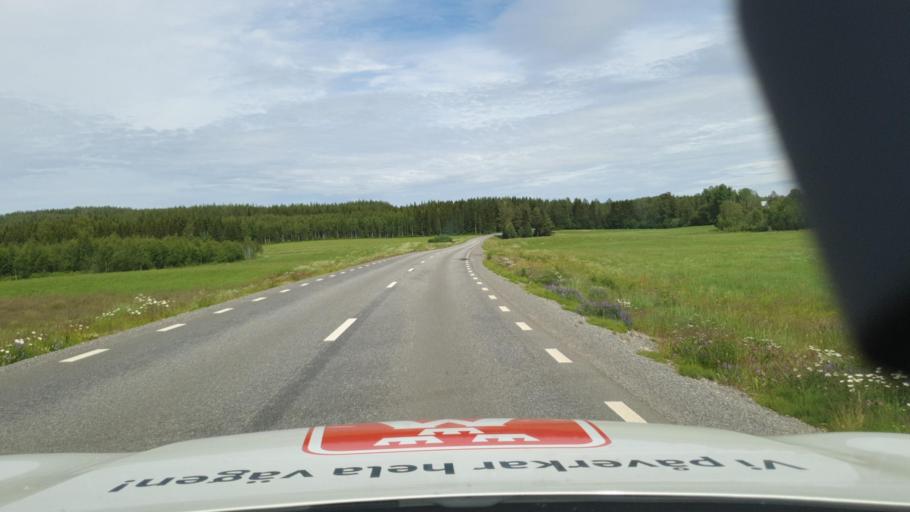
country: SE
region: Vaesterbotten
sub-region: Skelleftea Kommun
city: Burtraesk
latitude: 64.3806
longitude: 20.5139
